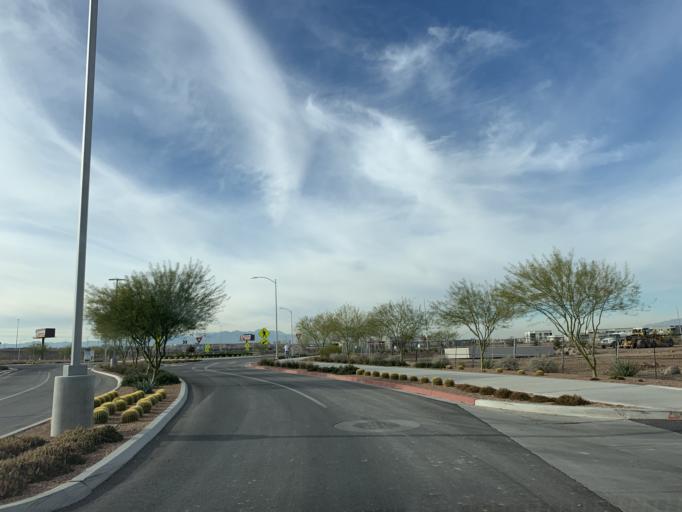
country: US
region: Nevada
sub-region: Clark County
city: Whitney
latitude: 36.0729
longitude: -115.0318
